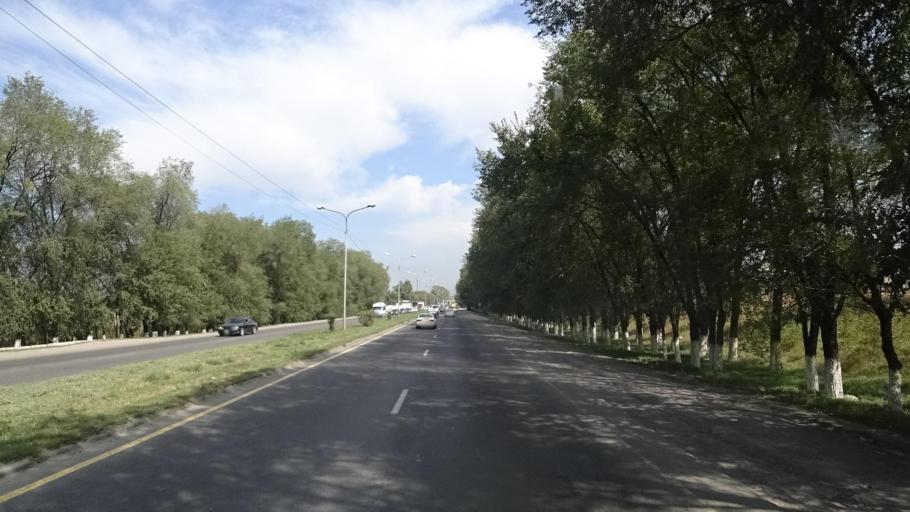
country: KZ
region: Almaty Oblysy
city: Burunday
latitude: 43.2252
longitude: 76.7300
